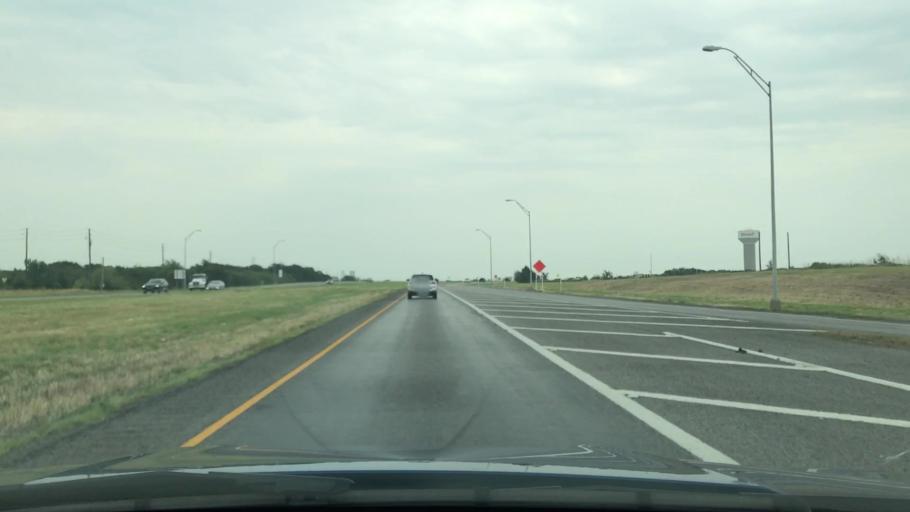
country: US
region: Texas
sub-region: Kaufman County
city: Terrell
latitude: 32.7195
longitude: -96.3169
